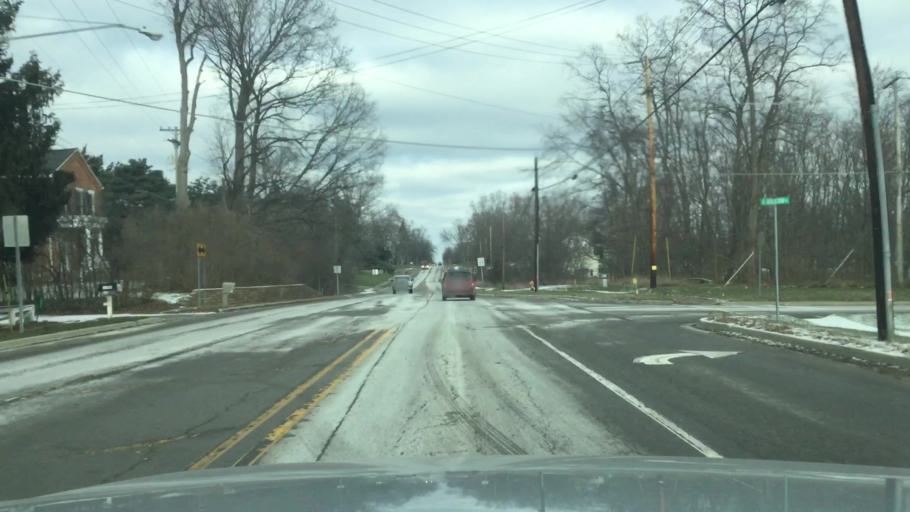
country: US
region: Michigan
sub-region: Genesee County
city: Linden
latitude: 42.8256
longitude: -83.7826
